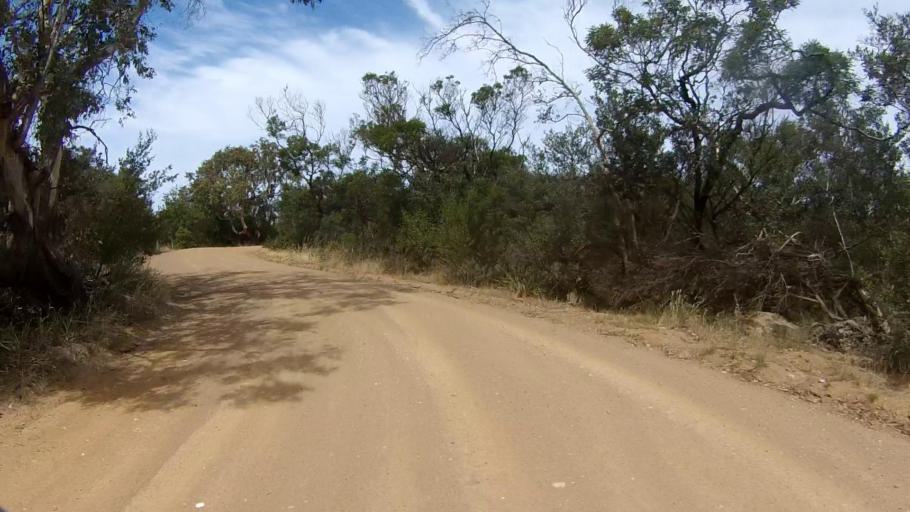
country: AU
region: Tasmania
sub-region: Clarence
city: Sandford
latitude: -43.0266
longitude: 147.4810
